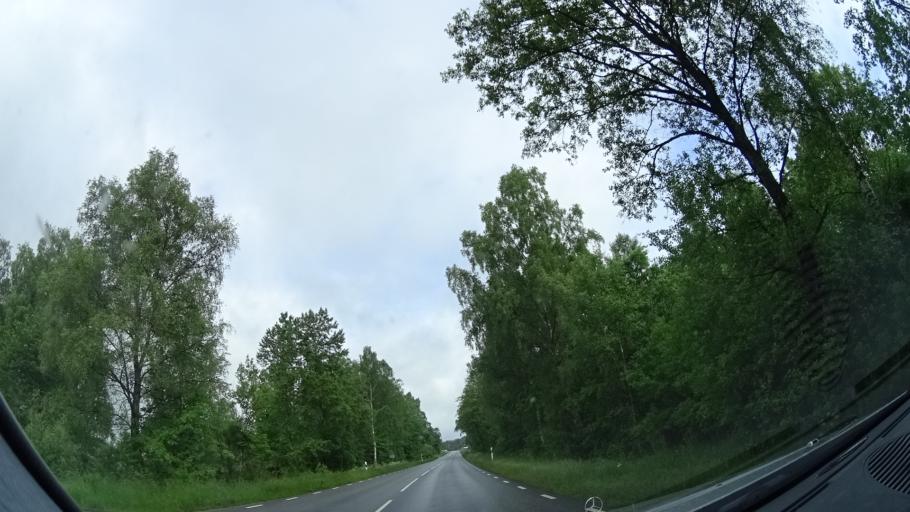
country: SE
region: Skane
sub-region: Hoors Kommun
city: Hoeoer
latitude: 55.9450
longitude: 13.4632
